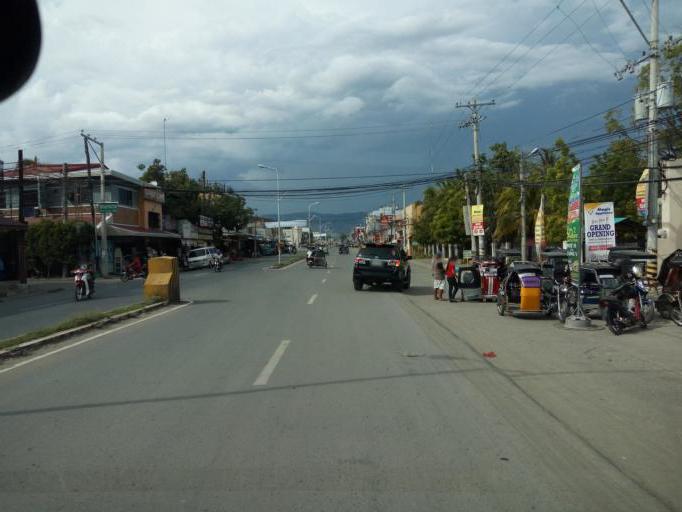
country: PH
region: Central Luzon
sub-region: Province of Nueva Ecija
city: Sibul
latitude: 15.7956
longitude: 120.9930
